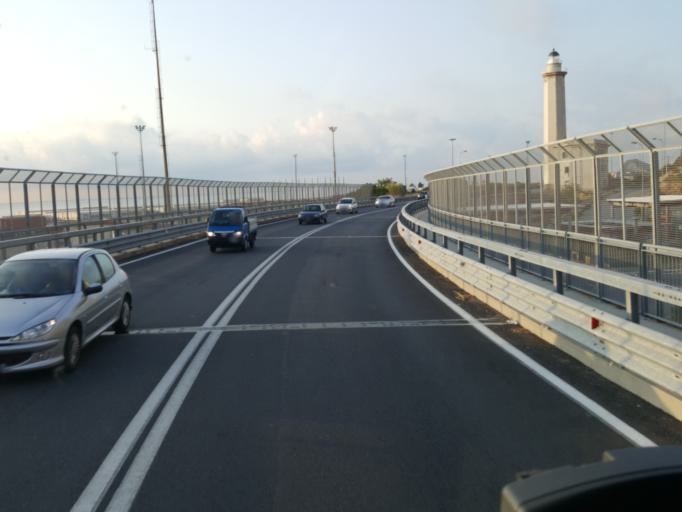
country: IT
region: Liguria
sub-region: Provincia di Savona
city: Bergeggi
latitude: 44.2600
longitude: 8.4529
